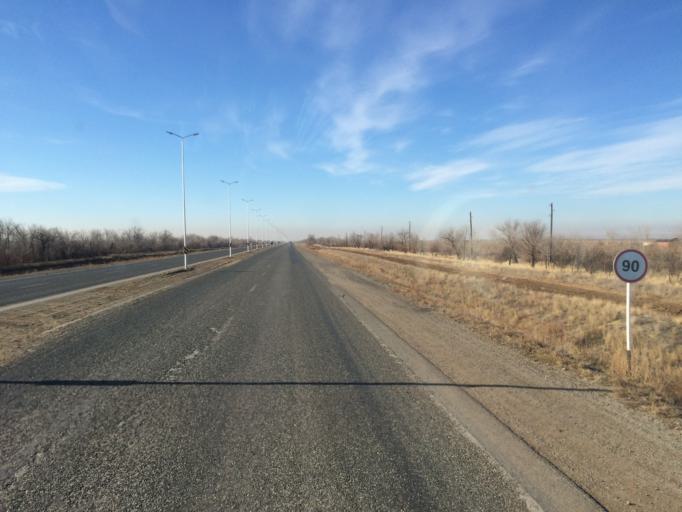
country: KZ
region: Aqtoebe
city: Aqtobe
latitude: 50.2913
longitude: 57.3535
